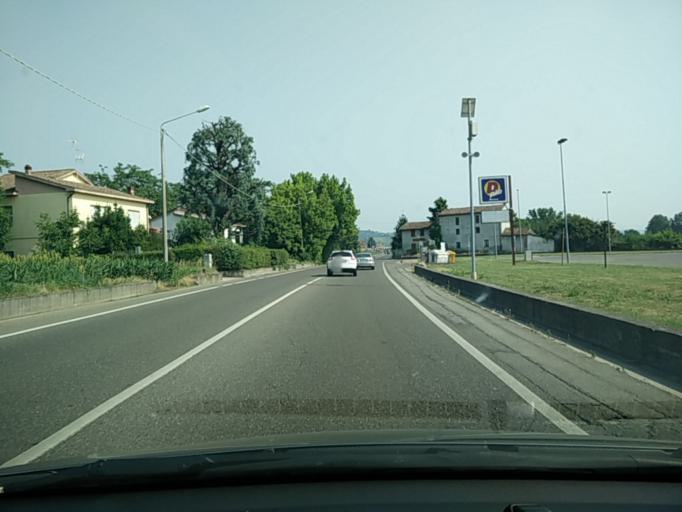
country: IT
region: Lombardy
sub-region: Provincia di Pavia
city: Campospinoso
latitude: 45.0938
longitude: 9.2529
